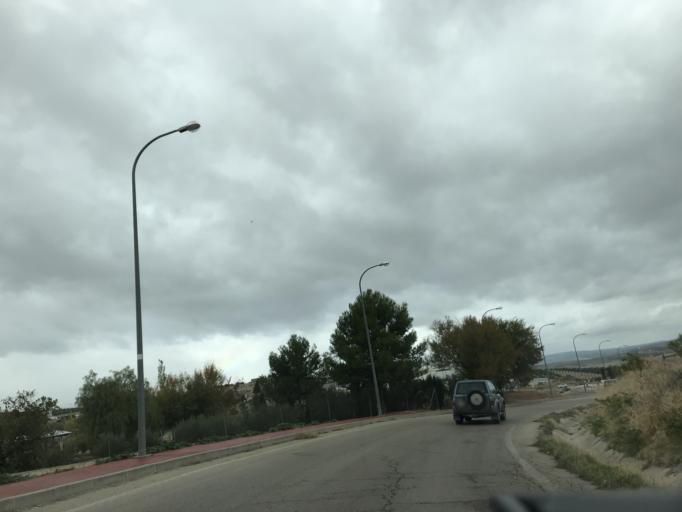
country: ES
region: Andalusia
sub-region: Provincia de Jaen
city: Peal de Becerro
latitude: 37.9160
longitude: -3.1317
